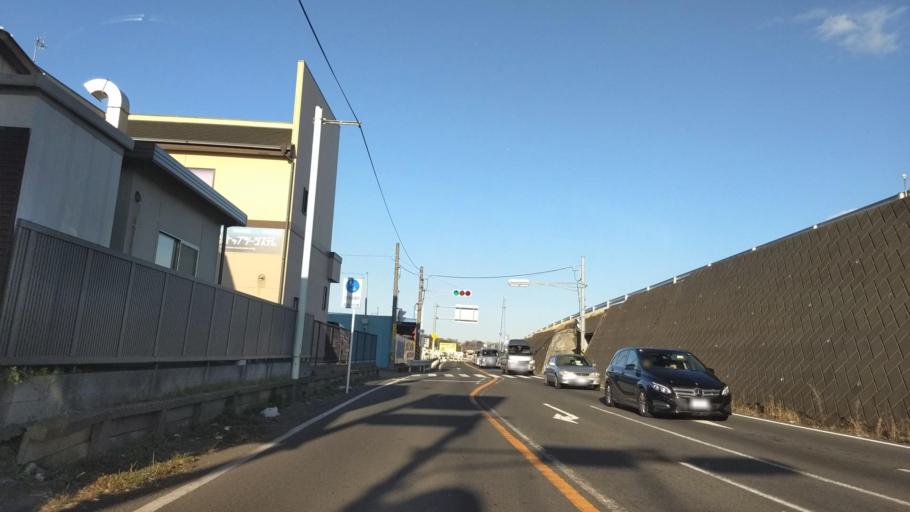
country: JP
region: Kanagawa
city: Isehara
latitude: 35.3698
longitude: 139.3116
